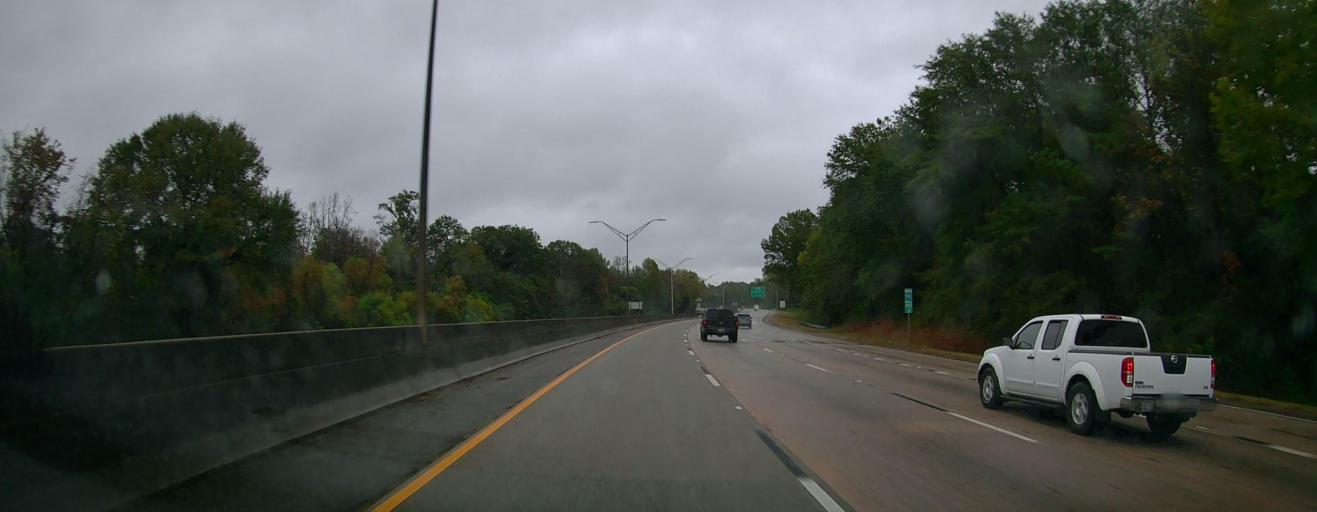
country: US
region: Georgia
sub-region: Bibb County
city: Macon
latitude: 32.7949
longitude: -83.6644
